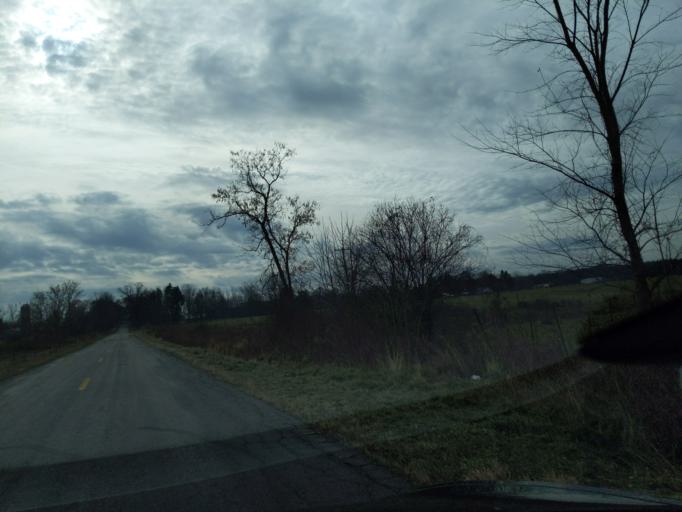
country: US
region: Michigan
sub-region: Ingham County
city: Leslie
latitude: 42.4626
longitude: -84.5019
